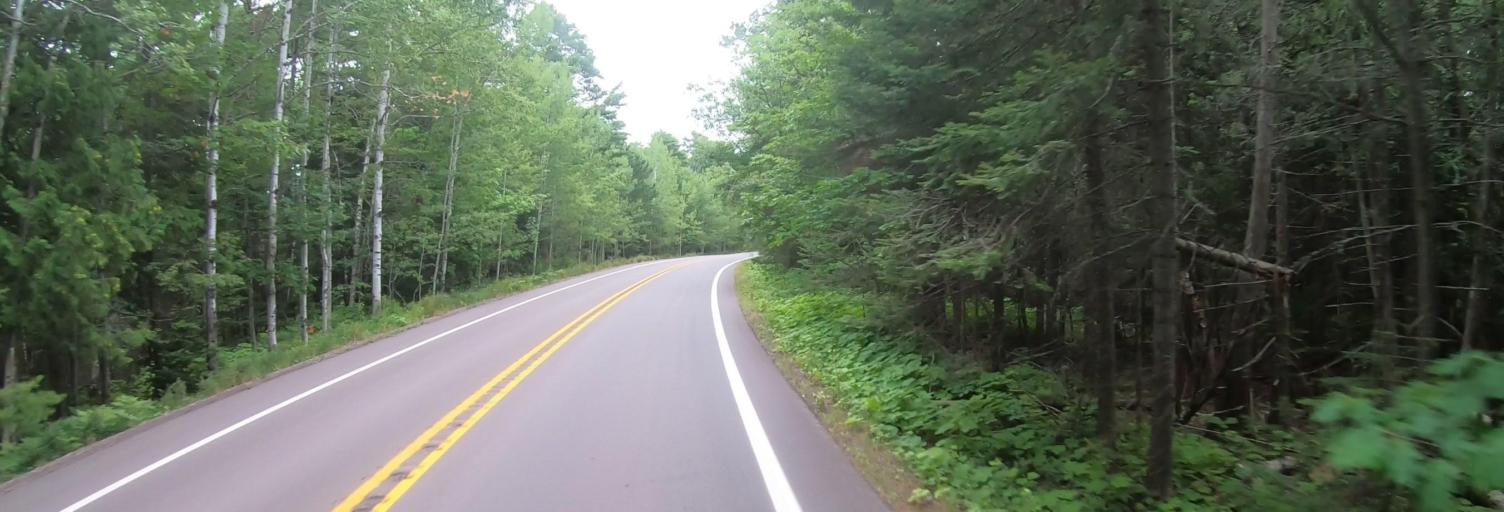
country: US
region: Michigan
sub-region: Keweenaw County
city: Eagle River
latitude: 47.4680
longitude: -87.8604
